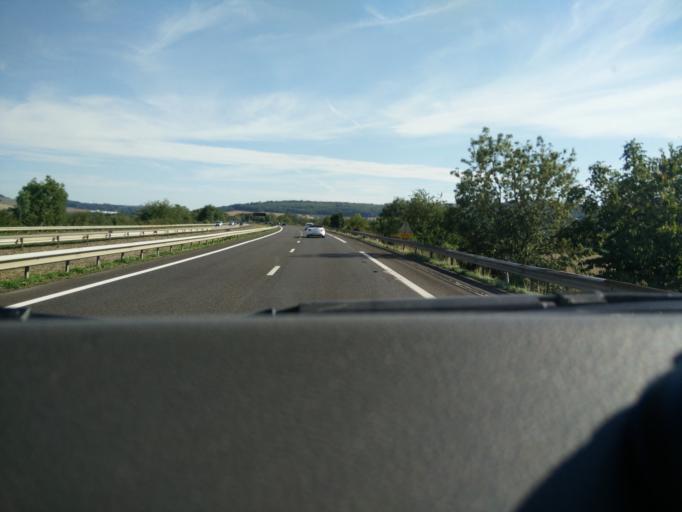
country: FR
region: Lorraine
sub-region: Departement de Meurthe-et-Moselle
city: Belleville
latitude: 48.8336
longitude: 6.0923
